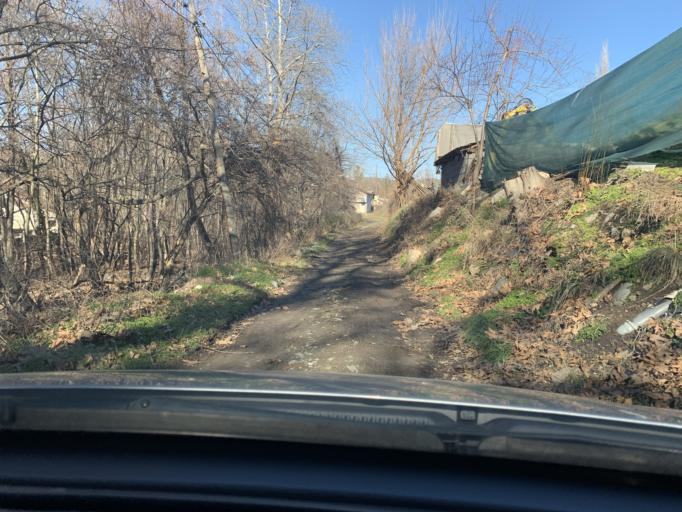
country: MK
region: Demir Kapija
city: Demir Kapija
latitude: 41.3869
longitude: 22.2224
